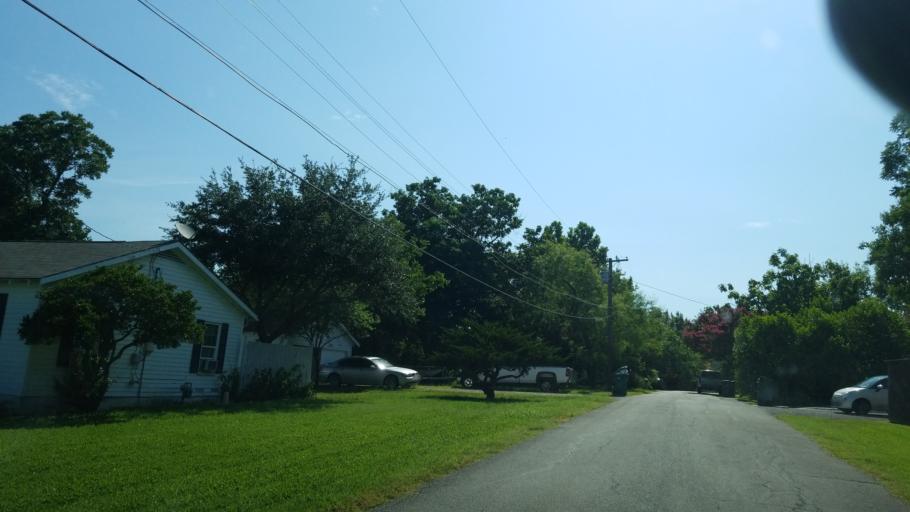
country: US
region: Texas
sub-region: Dallas County
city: Carrollton
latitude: 32.9575
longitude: -96.9000
